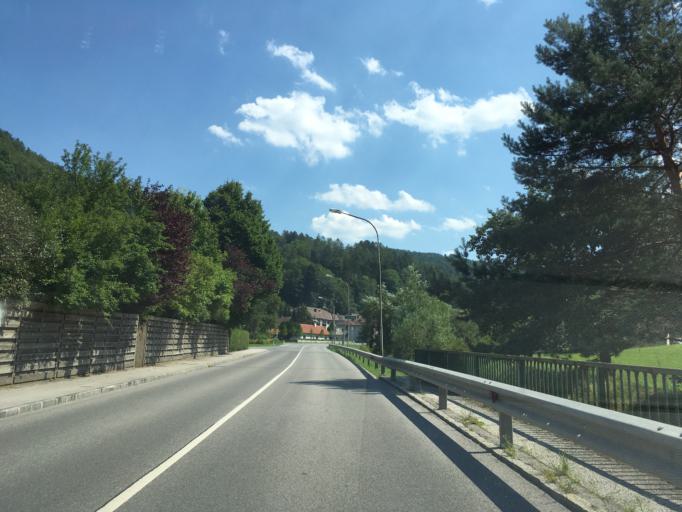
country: AT
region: Lower Austria
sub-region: Politischer Bezirk Neunkirchen
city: Edlitz
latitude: 47.5962
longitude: 16.1419
